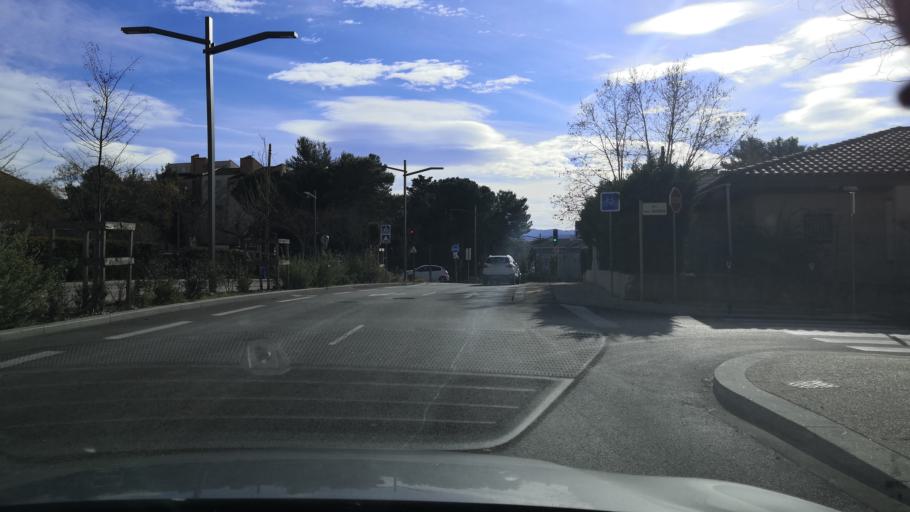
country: FR
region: Provence-Alpes-Cote d'Azur
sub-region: Departement des Bouches-du-Rhone
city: Aix-en-Provence
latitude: 43.5241
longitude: 5.4164
